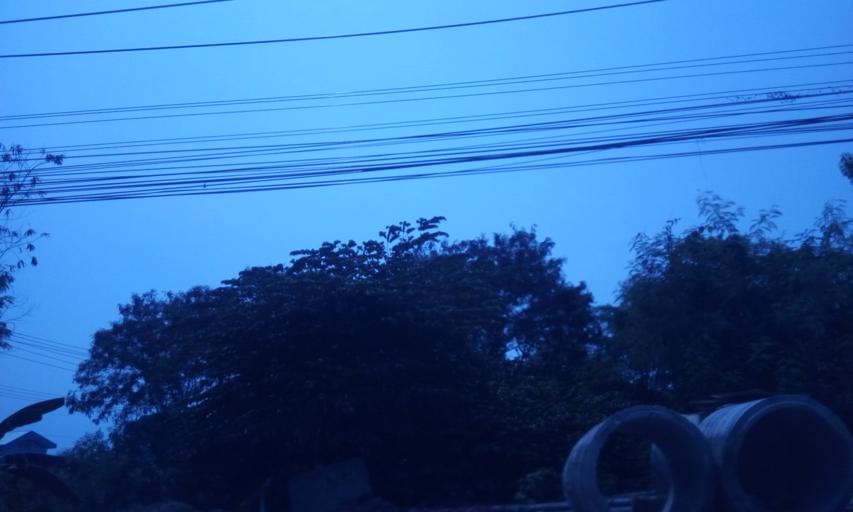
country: TH
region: Nonthaburi
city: Sai Noi
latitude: 13.9154
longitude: 100.3220
